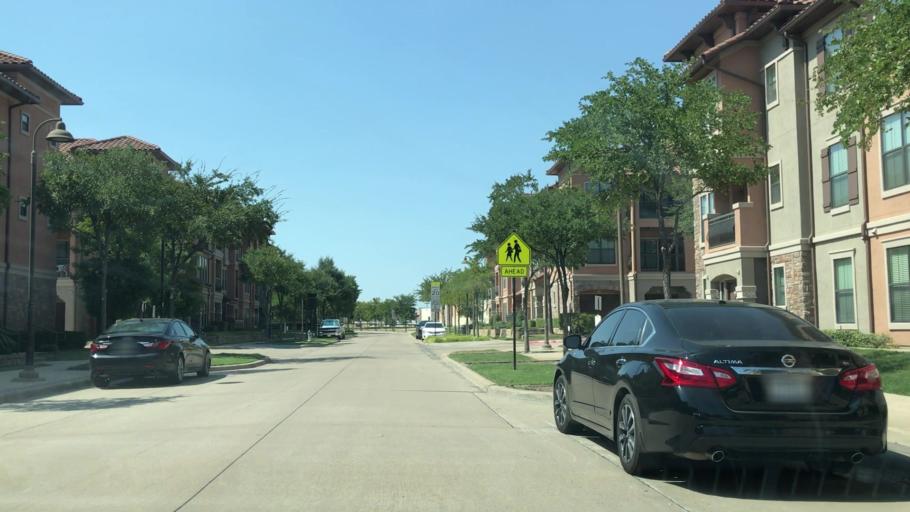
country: US
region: Texas
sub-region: Dallas County
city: Farmers Branch
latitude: 32.9008
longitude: -96.9370
